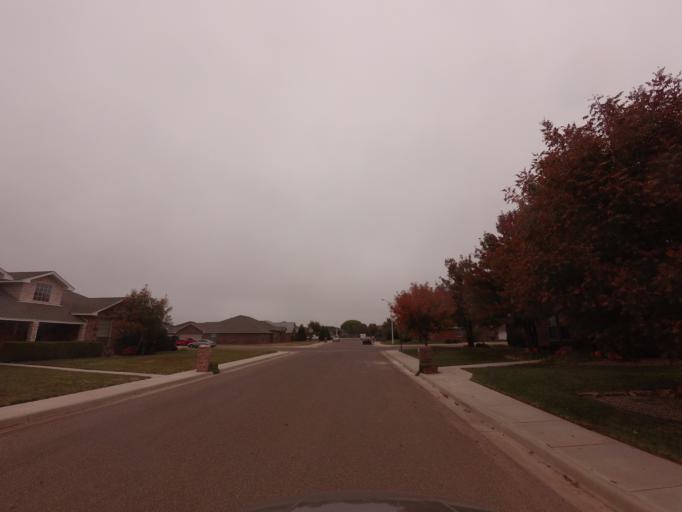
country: US
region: New Mexico
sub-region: Curry County
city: Clovis
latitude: 34.4303
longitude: -103.1701
